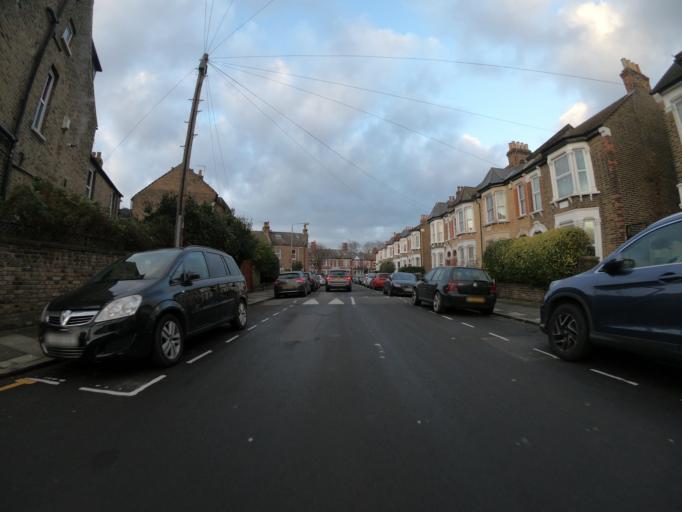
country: GB
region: England
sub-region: Greater London
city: Blackheath
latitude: 51.4775
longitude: 0.0240
